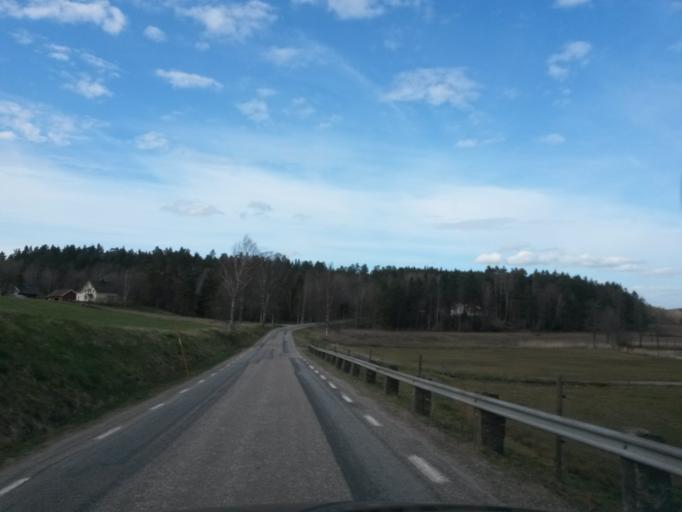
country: SE
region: Vaestra Goetaland
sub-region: Vargarda Kommun
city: Jonstorp
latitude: 57.9412
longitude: 12.7019
